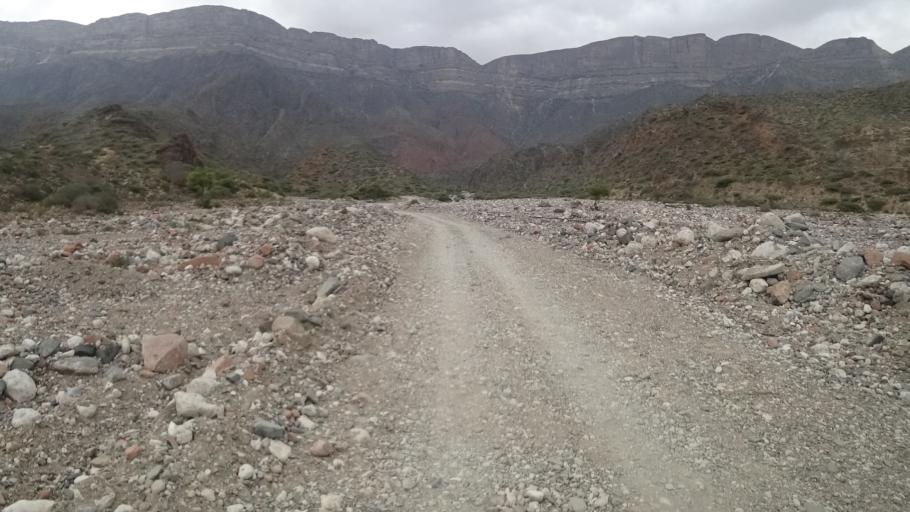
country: OM
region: Zufar
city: Salalah
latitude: 17.1771
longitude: 54.9496
